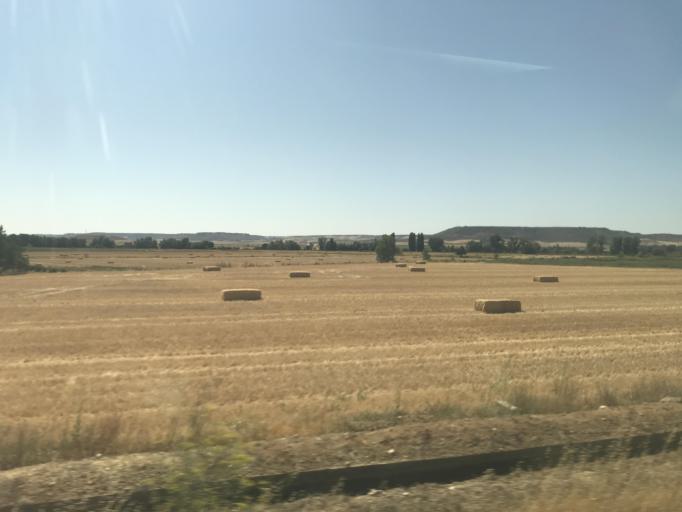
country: ES
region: Castille and Leon
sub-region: Provincia de Palencia
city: Reinoso de Cerrato
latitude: 42.0038
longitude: -4.3543
